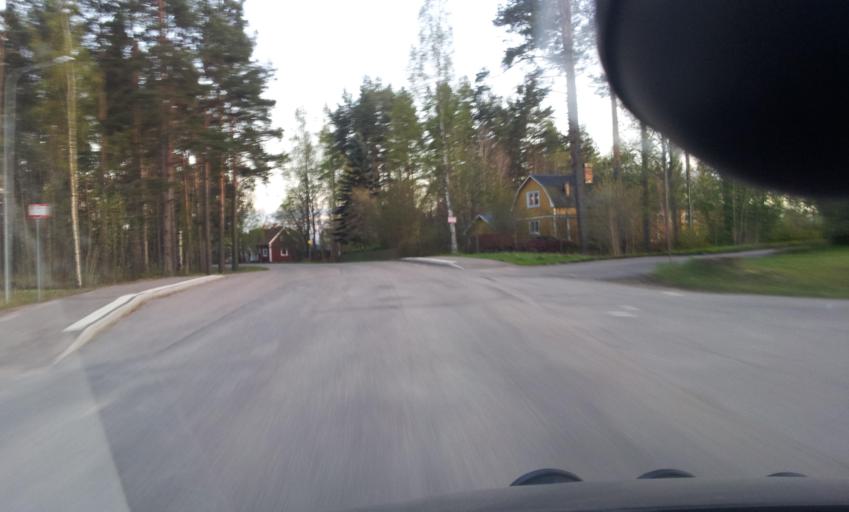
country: SE
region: Gaevleborg
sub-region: Bollnas Kommun
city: Bollnas
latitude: 61.3667
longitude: 16.4035
